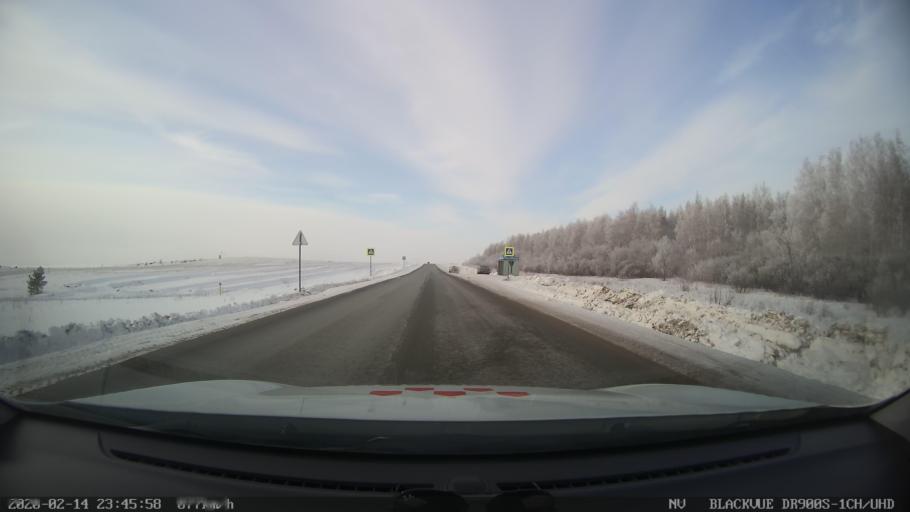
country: RU
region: Tatarstan
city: Kuybyshevskiy Zaton
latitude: 55.2269
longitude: 49.2313
